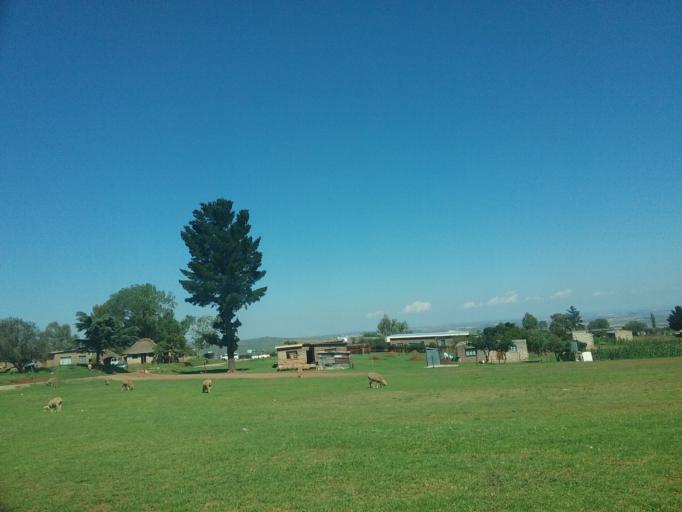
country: LS
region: Berea
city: Teyateyaneng
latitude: -29.2283
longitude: 27.8686
